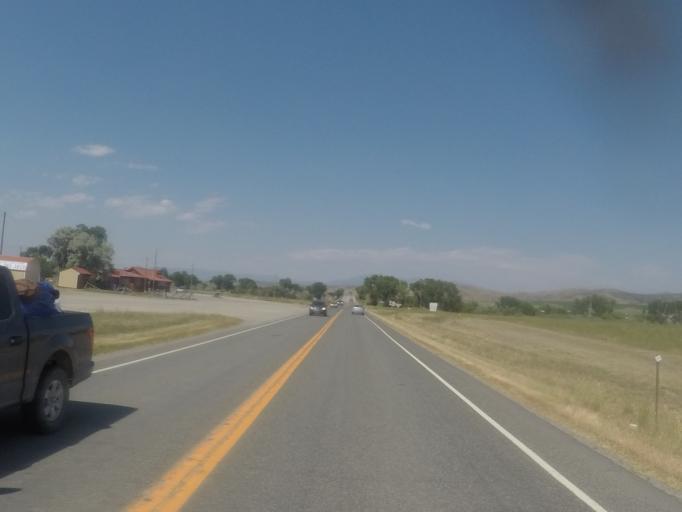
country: US
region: Montana
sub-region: Broadwater County
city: Townsend
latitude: 46.1702
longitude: -111.4483
